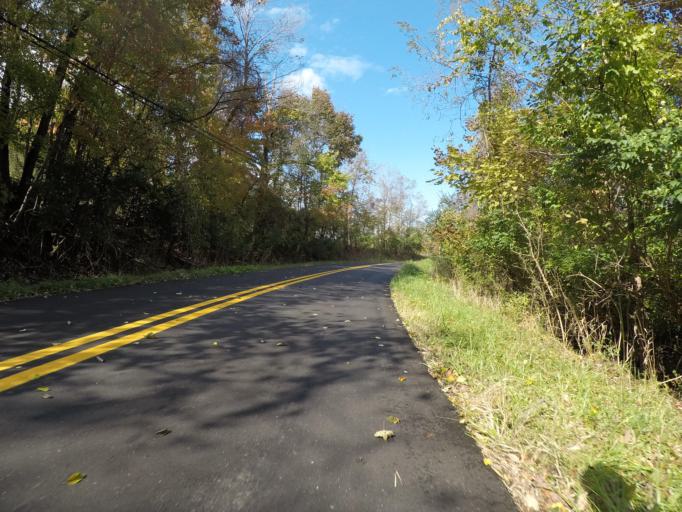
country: US
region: West Virginia
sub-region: Cabell County
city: Huntington
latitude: 38.3839
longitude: -82.4272
